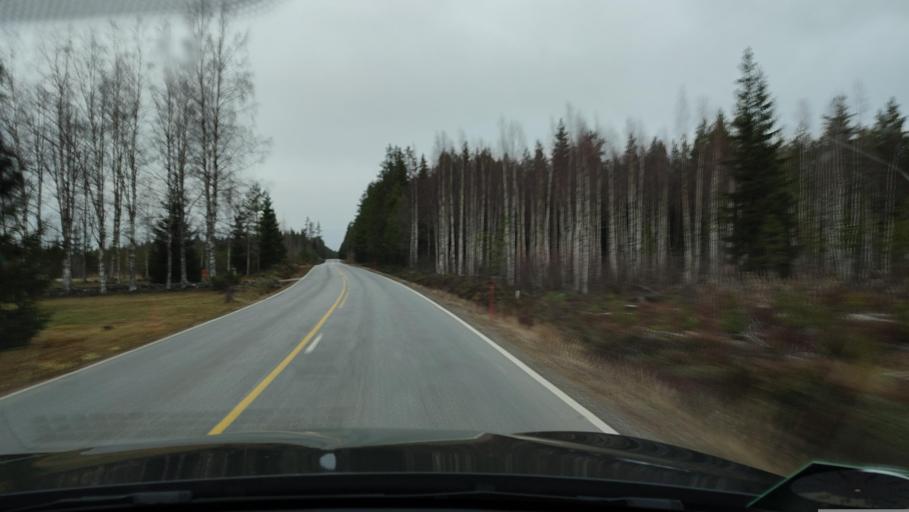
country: FI
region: Southern Ostrobothnia
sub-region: Suupohja
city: Karijoki
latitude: 62.2589
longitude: 21.7402
